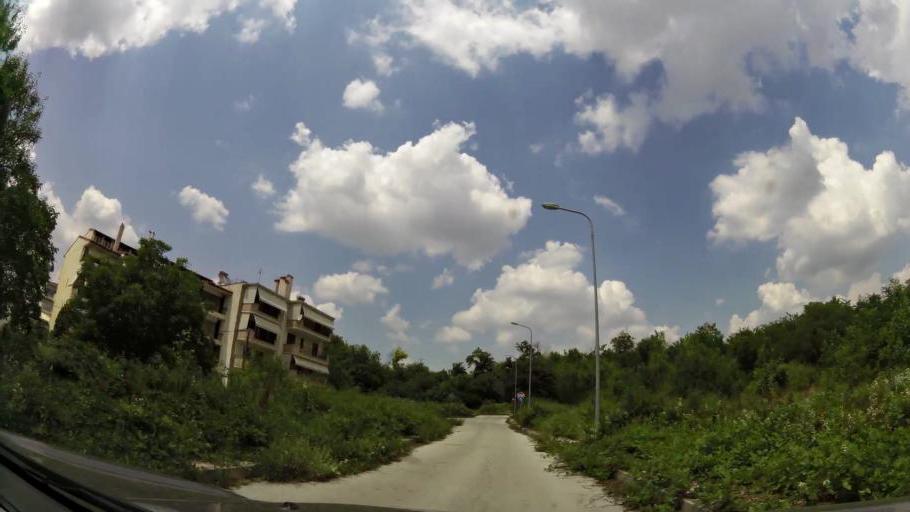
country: GR
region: West Macedonia
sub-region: Nomos Kozanis
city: Kozani
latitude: 40.2928
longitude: 21.7921
